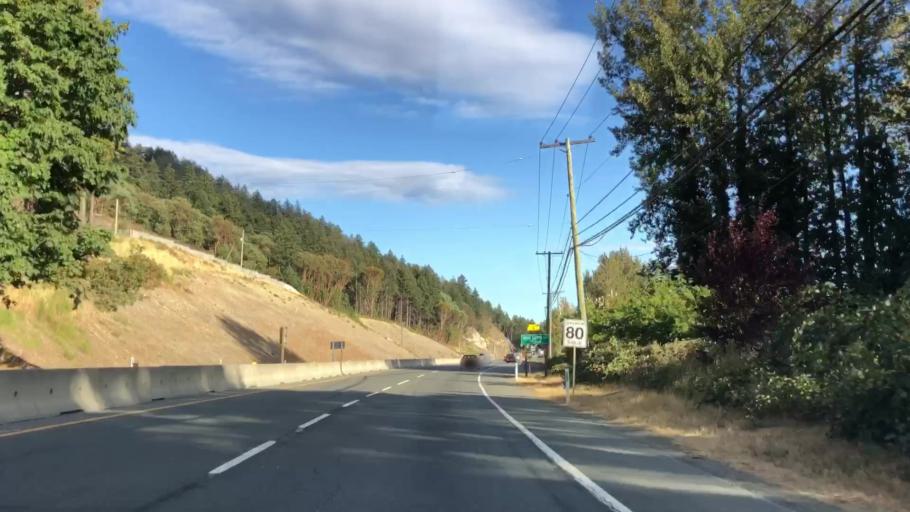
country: CA
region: British Columbia
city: Langford
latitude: 48.4595
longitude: -123.5411
